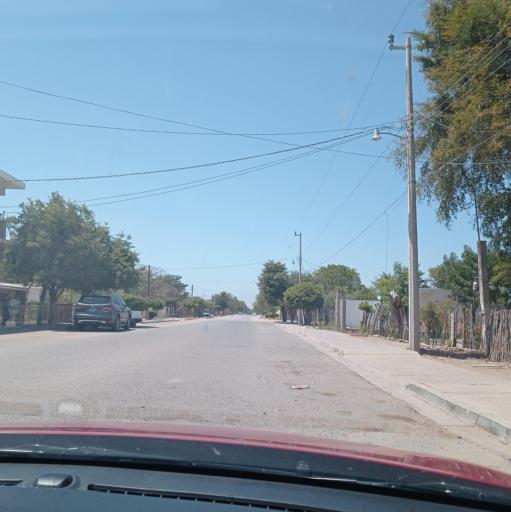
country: MX
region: Sinaloa
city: La Trinidad
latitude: 25.8074
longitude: -108.4812
